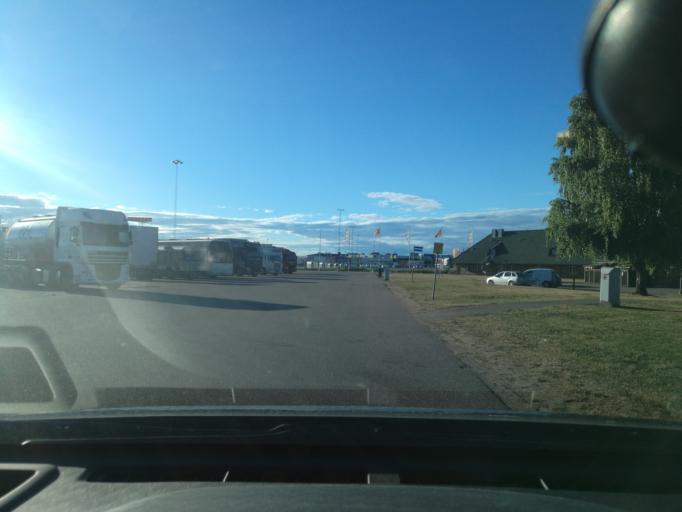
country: SE
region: Kalmar
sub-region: Kalmar Kommun
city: Kalmar
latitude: 56.6829
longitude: 16.3219
